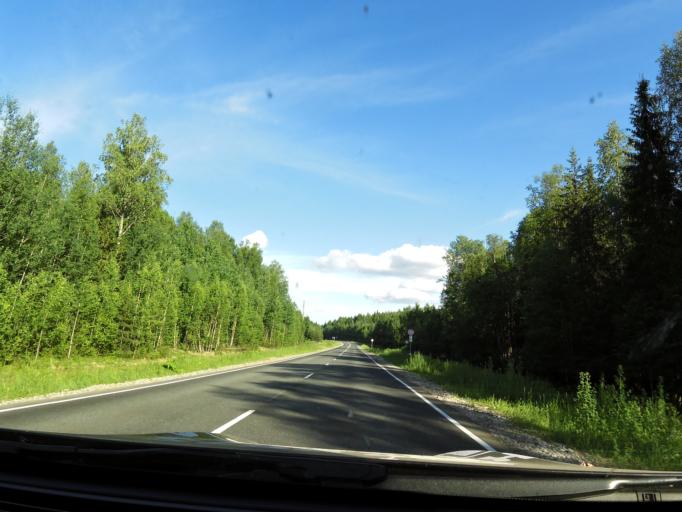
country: RU
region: Kirov
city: Chernaya Kholunitsa
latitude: 58.7783
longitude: 51.9202
